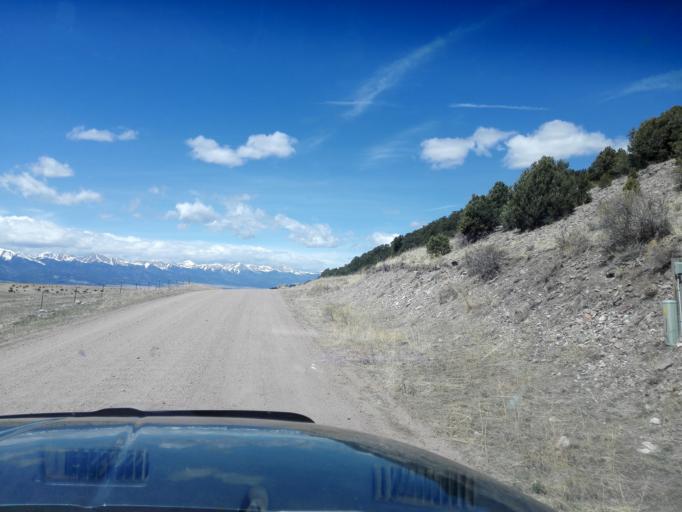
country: US
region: Colorado
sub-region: Custer County
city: Westcliffe
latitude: 37.9759
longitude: -105.2914
